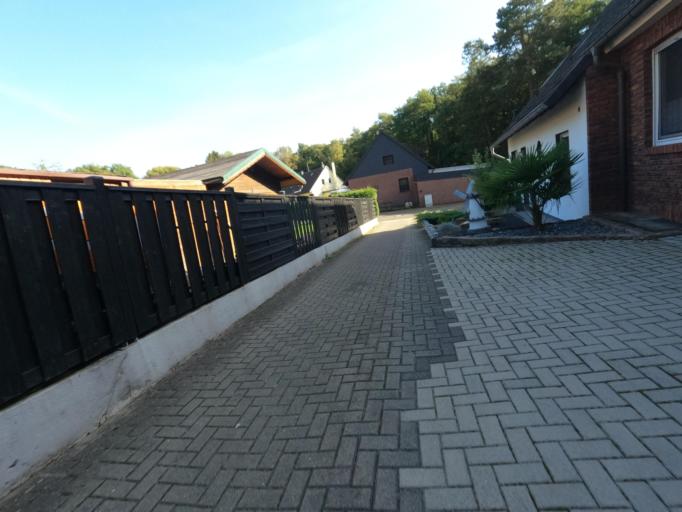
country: DE
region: North Rhine-Westphalia
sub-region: Regierungsbezirk Koln
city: Wassenberg
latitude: 51.1170
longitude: 6.1590
